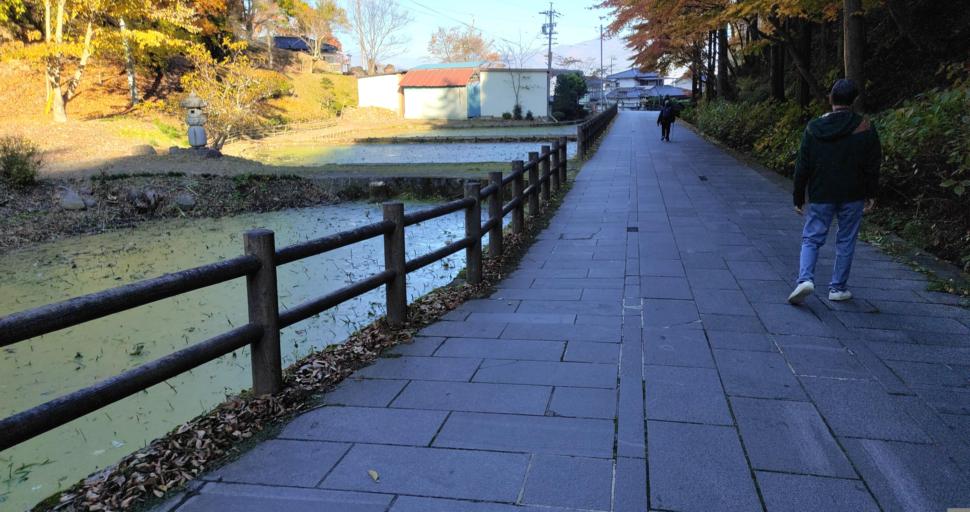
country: JP
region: Nagano
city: Kamimaruko
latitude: 36.3510
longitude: 138.1541
